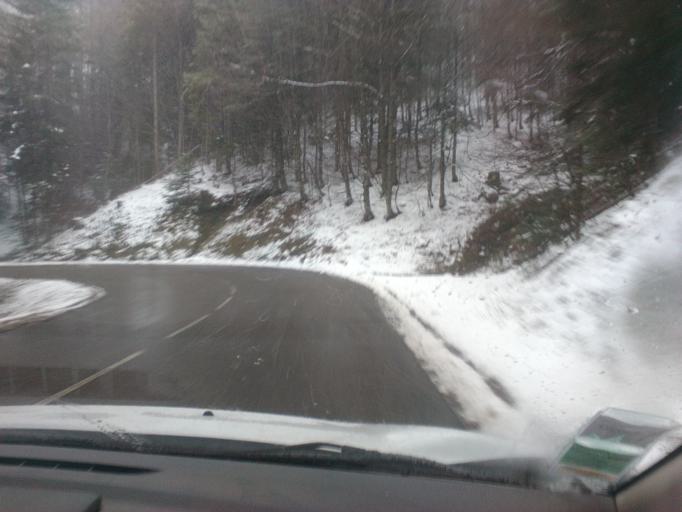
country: FR
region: Lorraine
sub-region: Departement des Vosges
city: Xonrupt-Longemer
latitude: 48.0635
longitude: 6.9954
